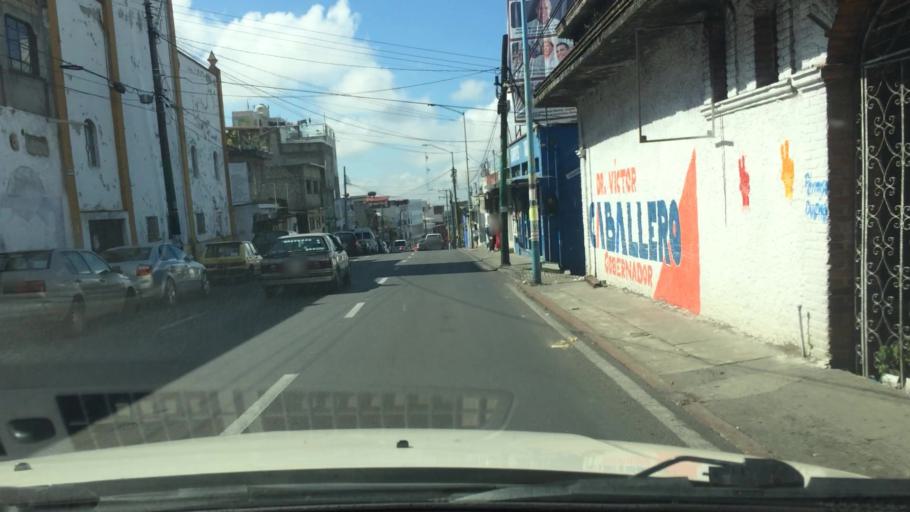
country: MX
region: Morelos
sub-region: Cuernavaca
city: Cuernavaca
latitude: 18.9387
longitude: -99.2412
